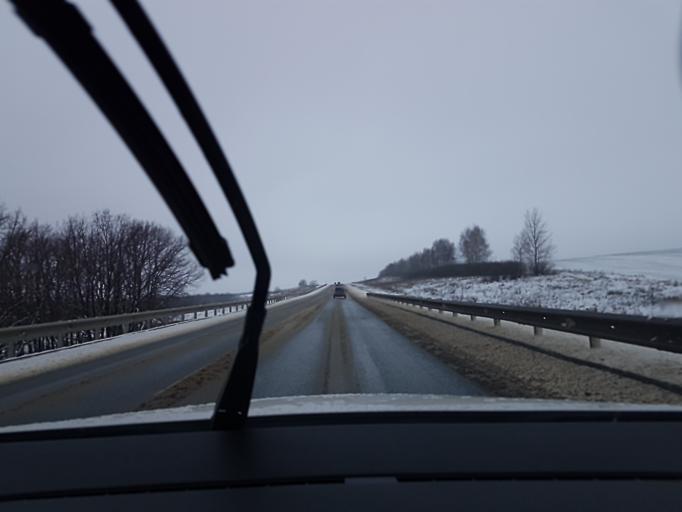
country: RU
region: Moskovskaya
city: Serebryanyye Prudy
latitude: 54.4116
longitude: 38.6568
